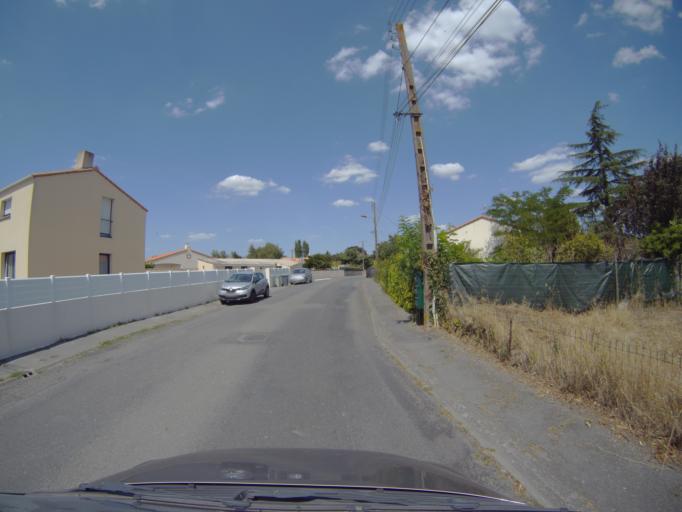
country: FR
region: Pays de la Loire
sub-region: Departement de la Loire-Atlantique
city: La Planche
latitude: 47.0151
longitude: -1.4322
